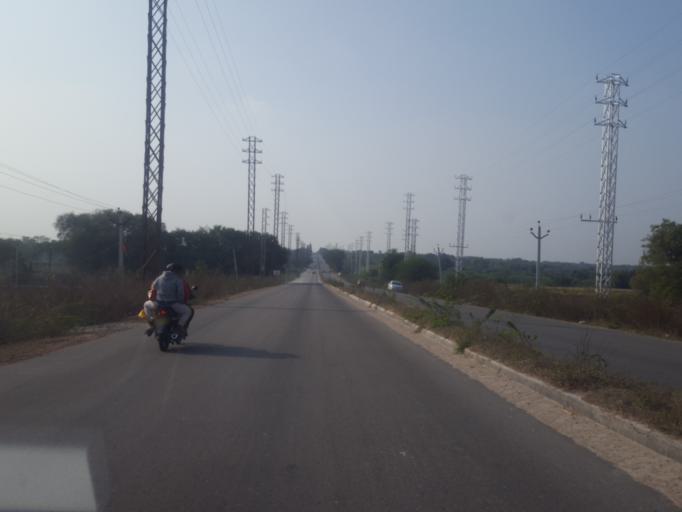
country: IN
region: Telangana
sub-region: Medak
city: Serilingampalle
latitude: 17.4107
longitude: 78.2715
